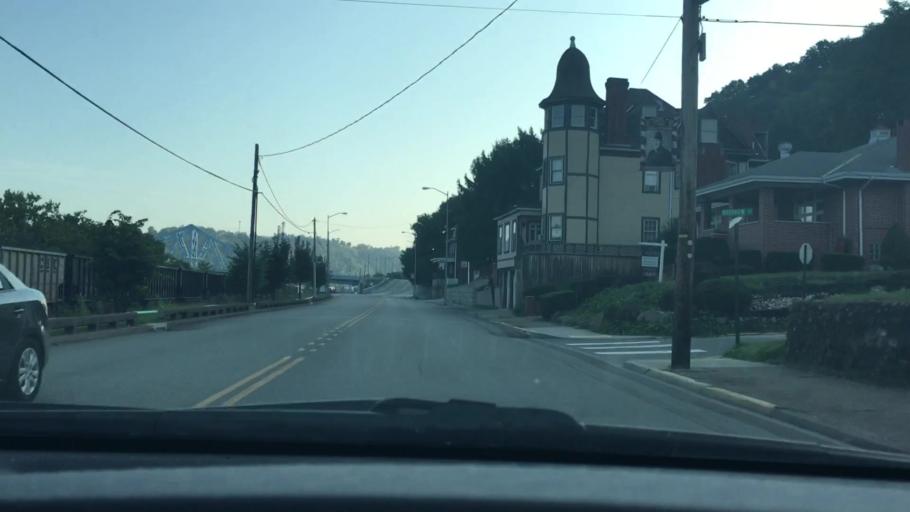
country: US
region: Pennsylvania
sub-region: Allegheny County
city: Dravosburg
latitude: 40.3412
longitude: -79.8870
